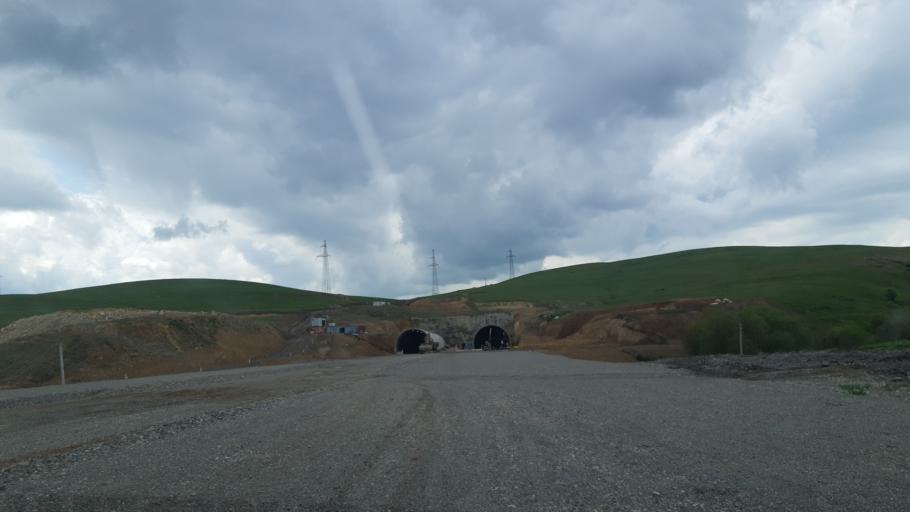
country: KZ
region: Ongtustik Qazaqstan
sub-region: Tulkibas Audany
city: Zhabagly
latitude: 42.5213
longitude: 70.5789
